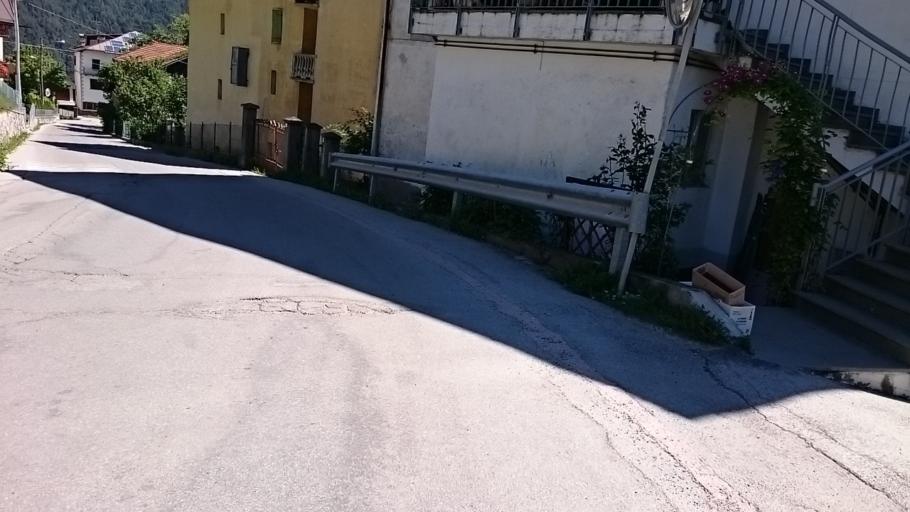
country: IT
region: Veneto
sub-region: Provincia di Belluno
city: Pieve di Cadore
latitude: 46.4245
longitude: 12.3735
